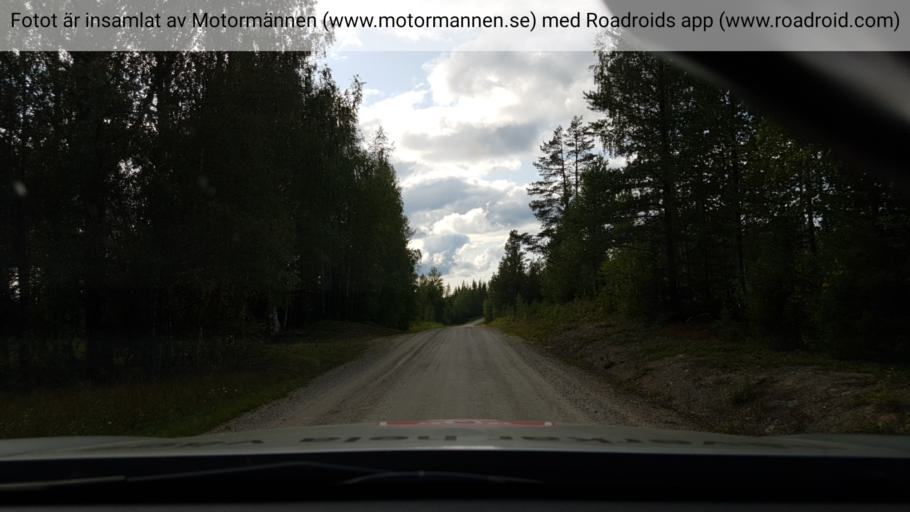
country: SE
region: Vaesterbotten
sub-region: Lycksele Kommun
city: Lycksele
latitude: 64.7079
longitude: 18.8435
